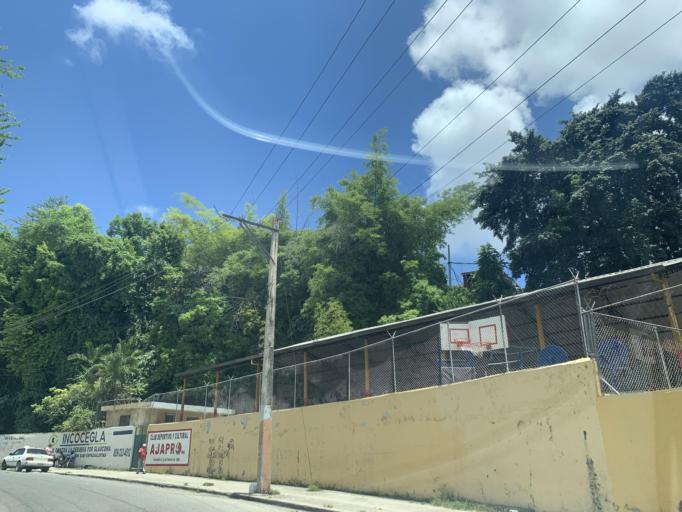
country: DO
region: Nacional
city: La Agustina
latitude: 18.4977
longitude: -69.9319
